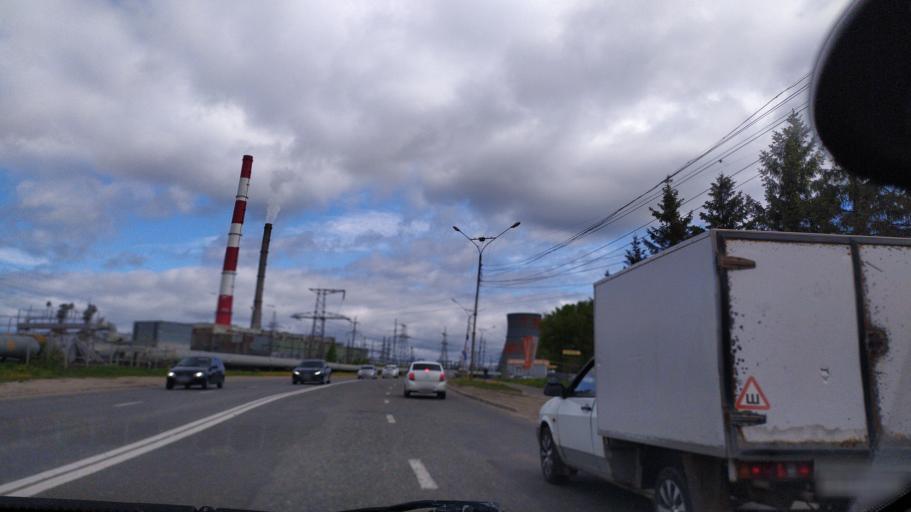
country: RU
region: Chuvashia
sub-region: Cheboksarskiy Rayon
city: Cheboksary
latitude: 56.1186
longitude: 47.3019
